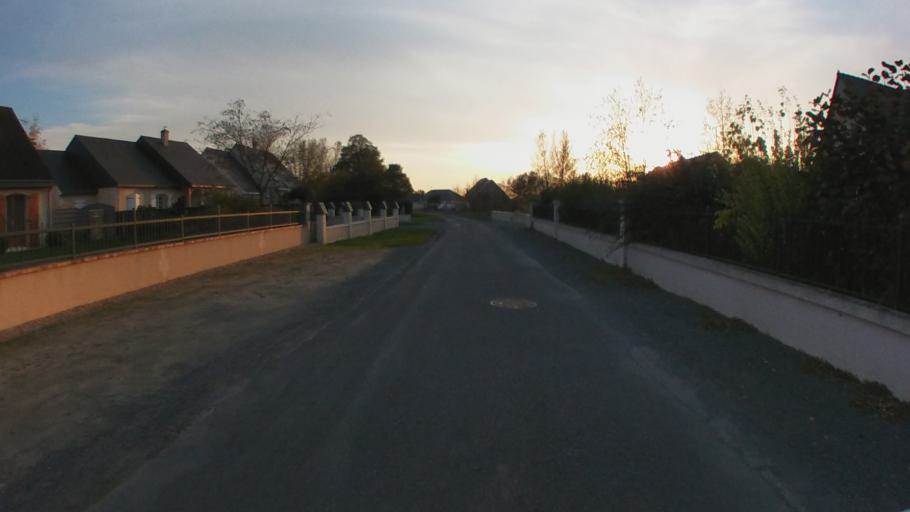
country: FR
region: Pays de la Loire
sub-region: Departement de Maine-et-Loire
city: Vivy
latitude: 47.3274
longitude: -0.0610
